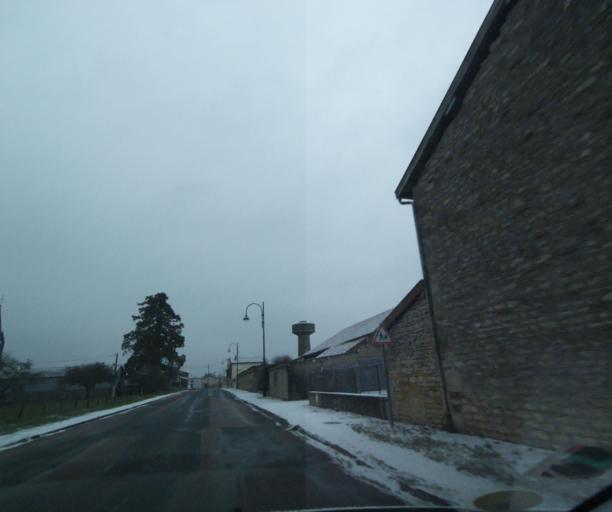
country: FR
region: Champagne-Ardenne
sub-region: Departement de la Haute-Marne
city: Wassy
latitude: 48.4304
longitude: 5.0011
